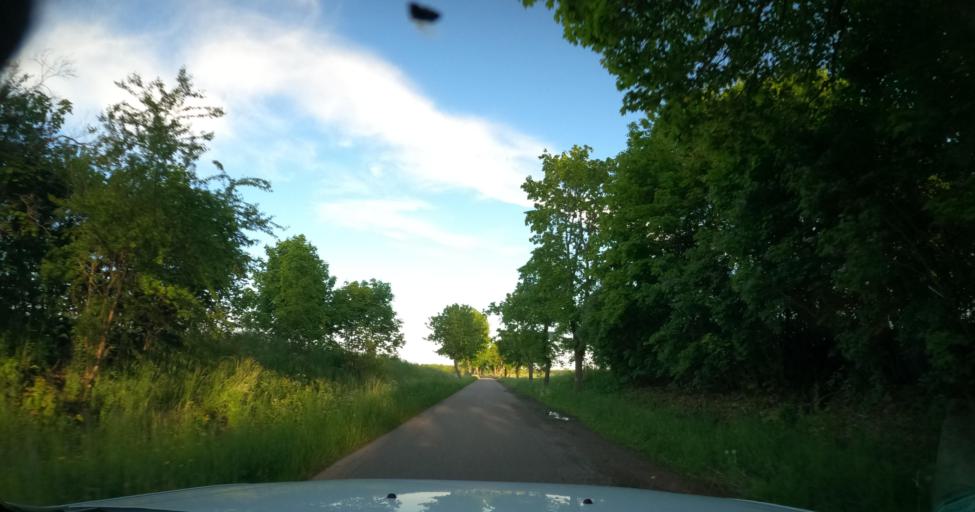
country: PL
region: Warmian-Masurian Voivodeship
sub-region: Powiat lidzbarski
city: Orneta
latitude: 54.1736
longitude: 20.1617
